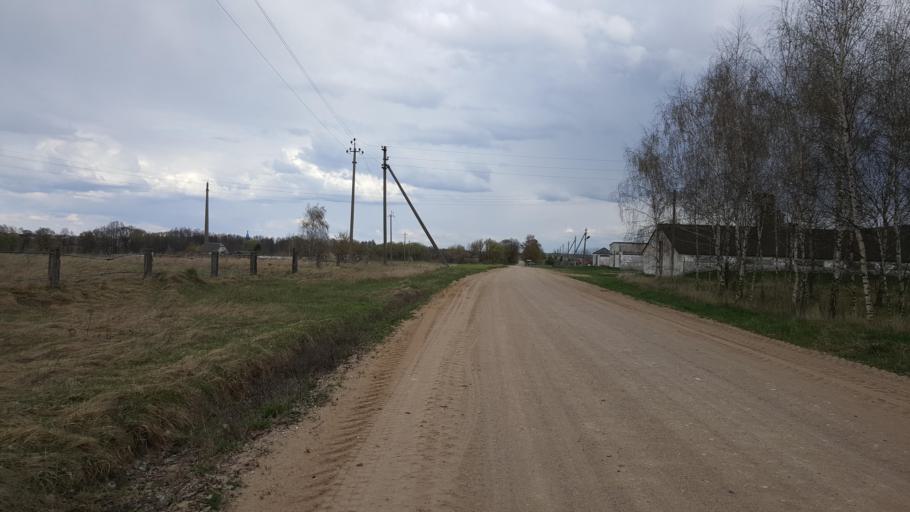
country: BY
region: Brest
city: Kamyanyets
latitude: 52.3952
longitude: 23.7492
